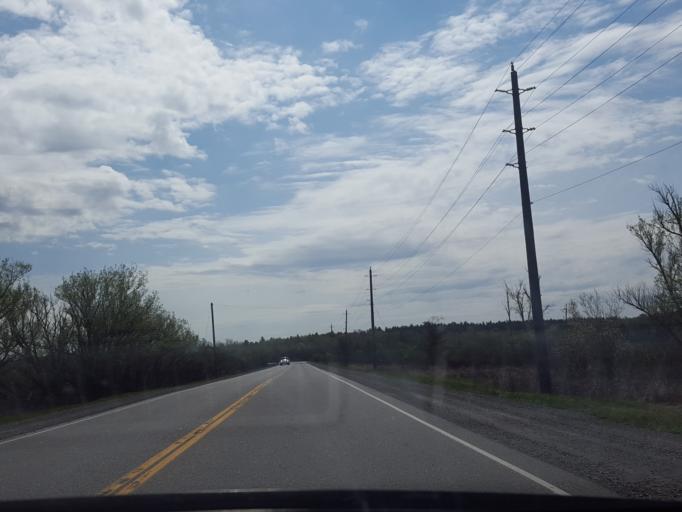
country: CA
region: Ontario
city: Oshawa
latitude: 44.1063
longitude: -78.8942
